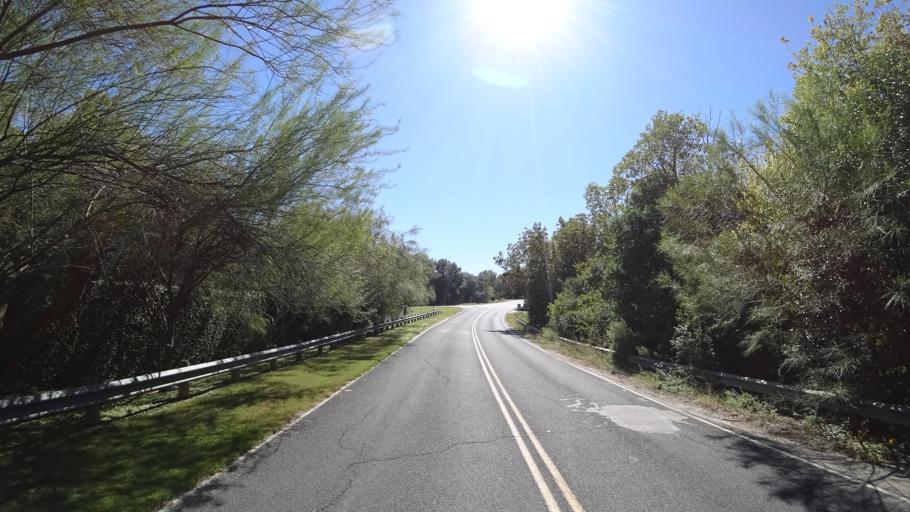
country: US
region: Texas
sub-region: Travis County
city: West Lake Hills
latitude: 30.3045
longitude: -97.7870
